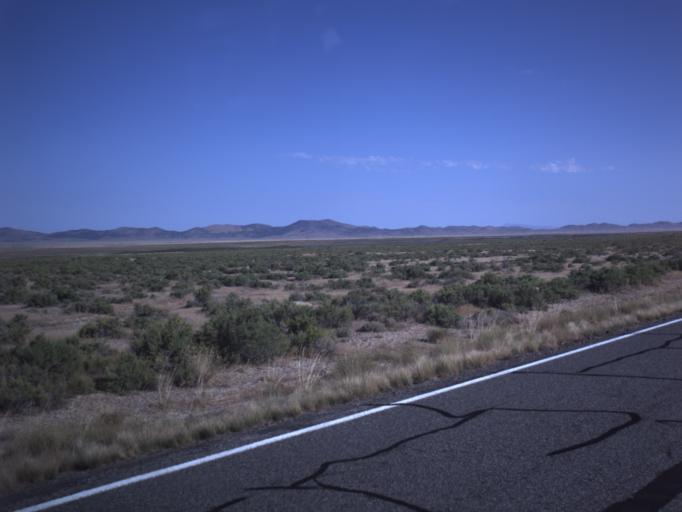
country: US
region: Utah
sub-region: Beaver County
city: Milford
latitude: 38.5082
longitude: -112.9911
